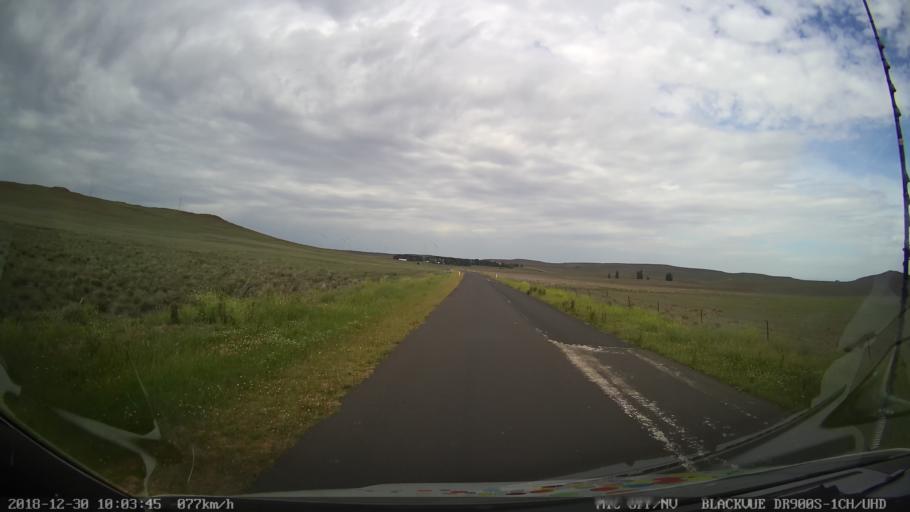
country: AU
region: New South Wales
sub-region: Cooma-Monaro
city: Cooma
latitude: -36.5162
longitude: 149.1532
